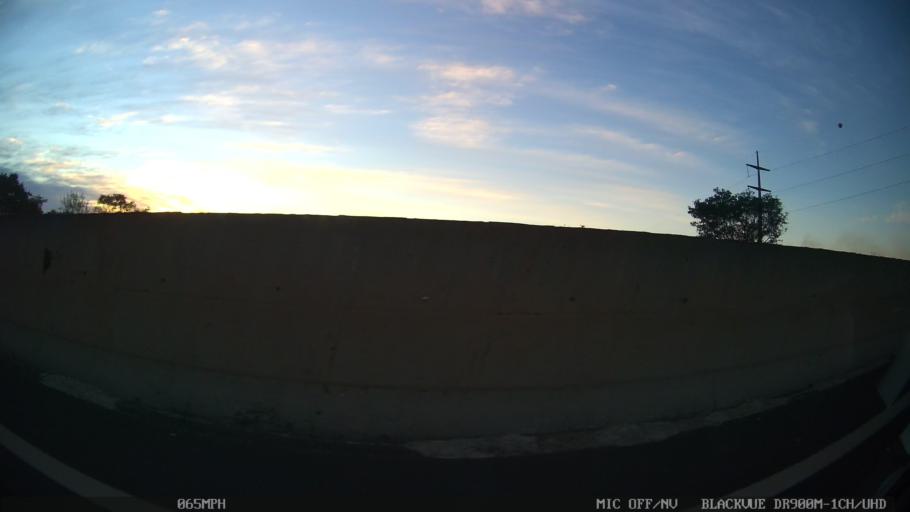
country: BR
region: Sao Paulo
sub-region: Catanduva
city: Catanduva
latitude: -21.1183
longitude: -48.9846
